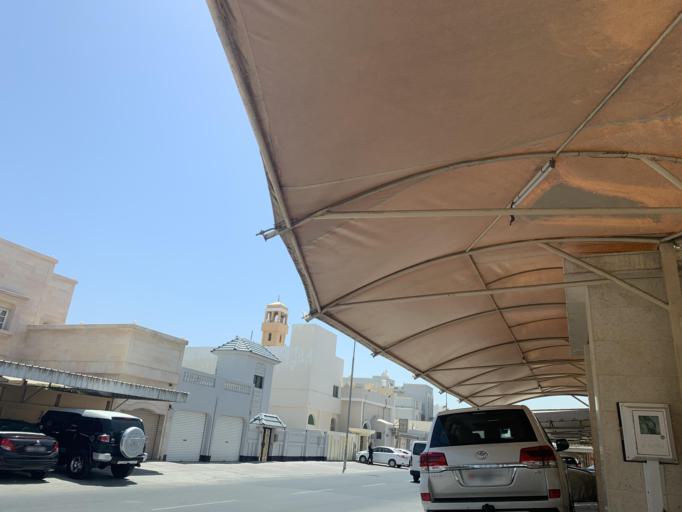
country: BH
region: Northern
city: Ar Rifa'
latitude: 26.1328
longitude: 50.5790
